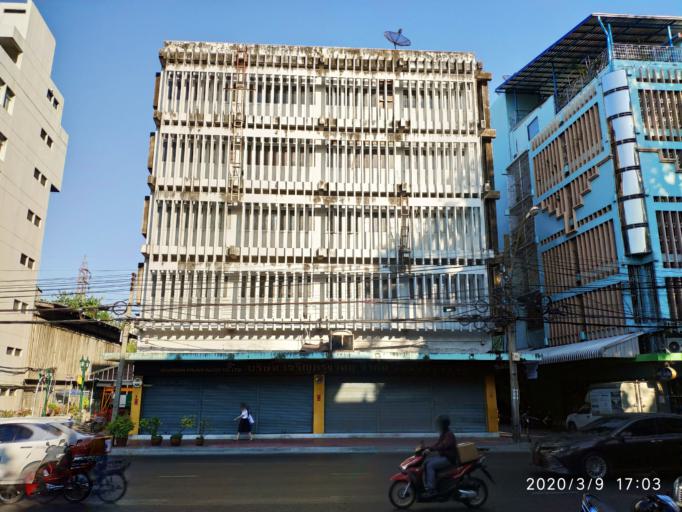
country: TH
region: Bangkok
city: Bangkok
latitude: 13.7478
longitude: 100.5033
